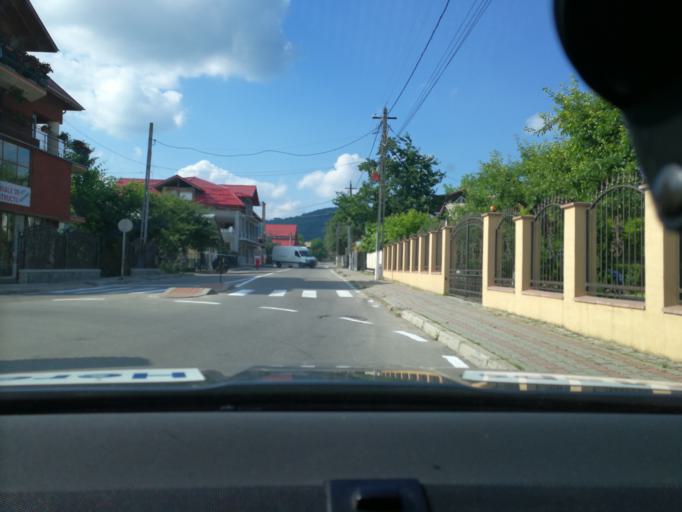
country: RO
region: Prahova
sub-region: Comuna Cornu
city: Cornu de Jos
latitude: 45.1580
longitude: 25.7024
